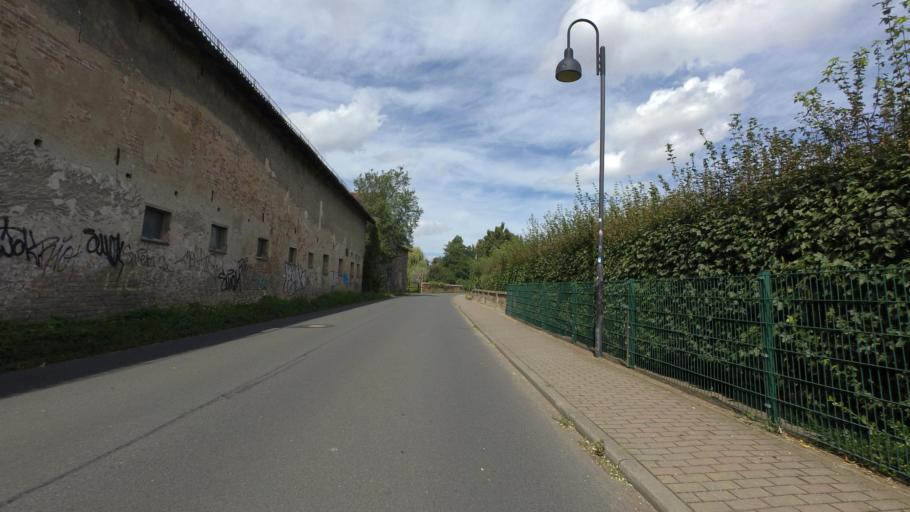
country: DE
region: Brandenburg
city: Gross Kreutz
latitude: 52.4059
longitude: 12.7765
